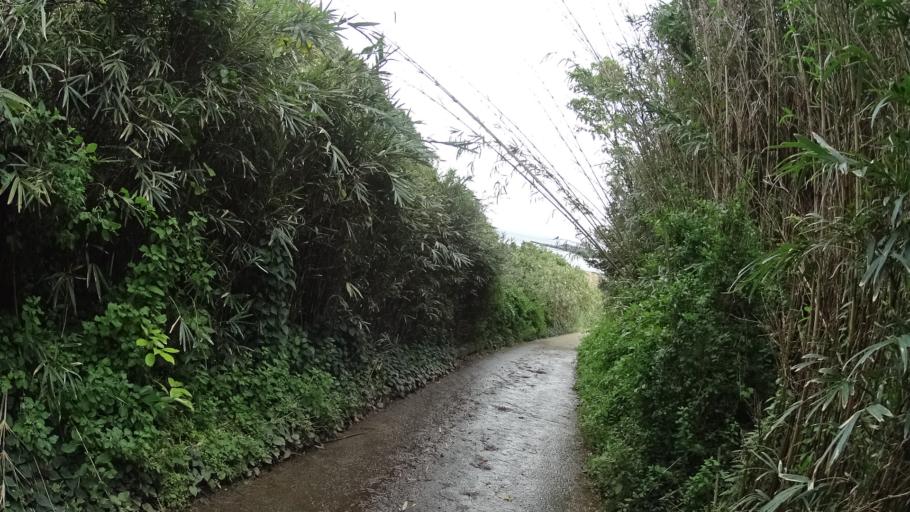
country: JP
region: Kanagawa
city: Miura
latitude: 35.1411
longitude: 139.6607
